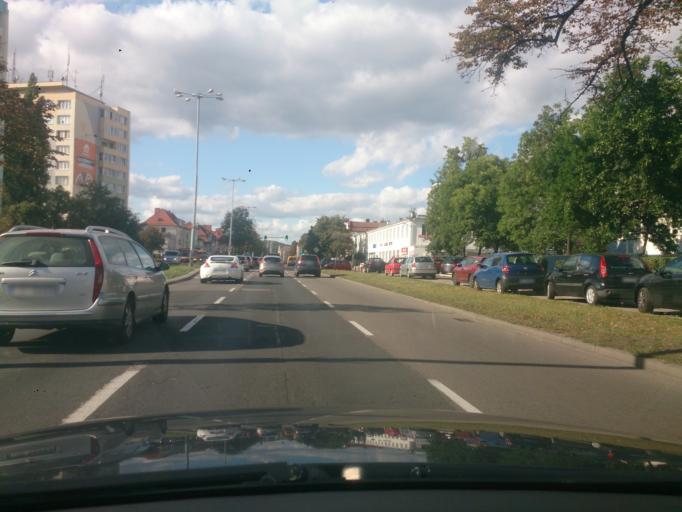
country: PL
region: Pomeranian Voivodeship
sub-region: Sopot
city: Sopot
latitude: 54.4049
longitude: 18.5714
